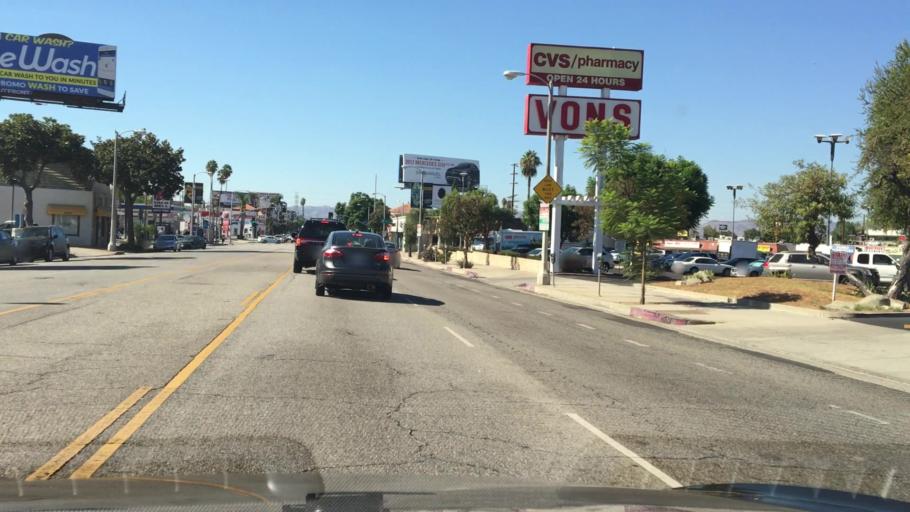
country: US
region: California
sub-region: Los Angeles County
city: Northridge
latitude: 34.1682
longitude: -118.5343
